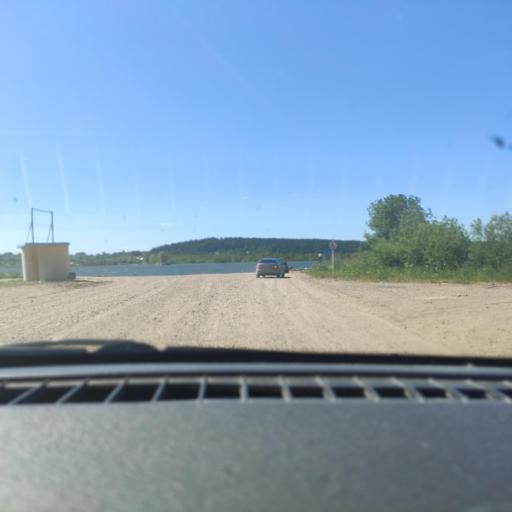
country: RU
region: Perm
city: Verkhnechusovskiye Gorodki
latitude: 58.1919
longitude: 57.1295
